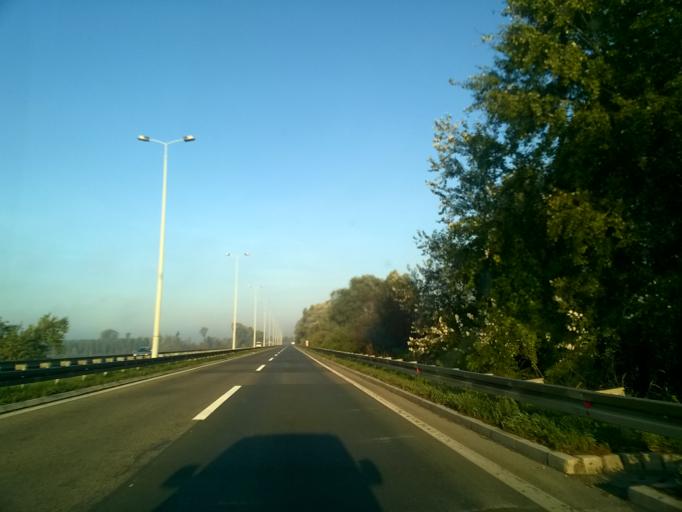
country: RS
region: Autonomna Pokrajina Vojvodina
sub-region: Juznobanatski Okrug
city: Pancevo
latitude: 44.8605
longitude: 20.5925
